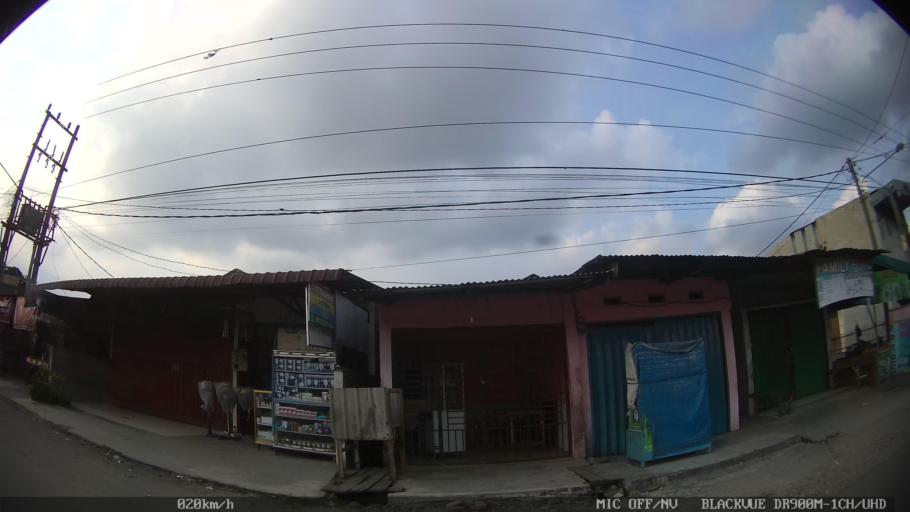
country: ID
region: North Sumatra
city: Medan
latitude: 3.5813
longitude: 98.7377
